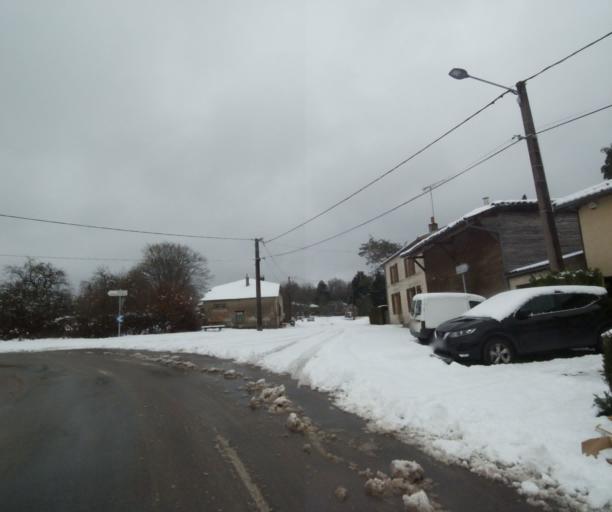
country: FR
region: Champagne-Ardenne
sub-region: Departement de la Haute-Marne
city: Laneuville-a-Remy
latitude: 48.4754
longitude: 4.8865
